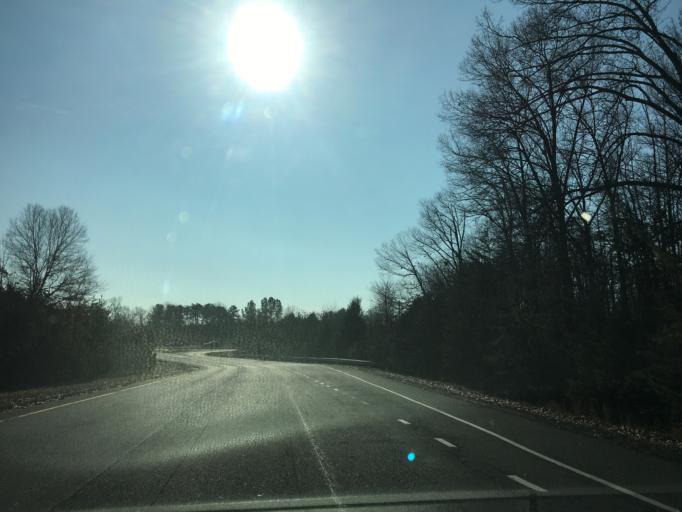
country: US
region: Virginia
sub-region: Fairfax County
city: Fairfax Station
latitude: 38.8296
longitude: -77.3686
